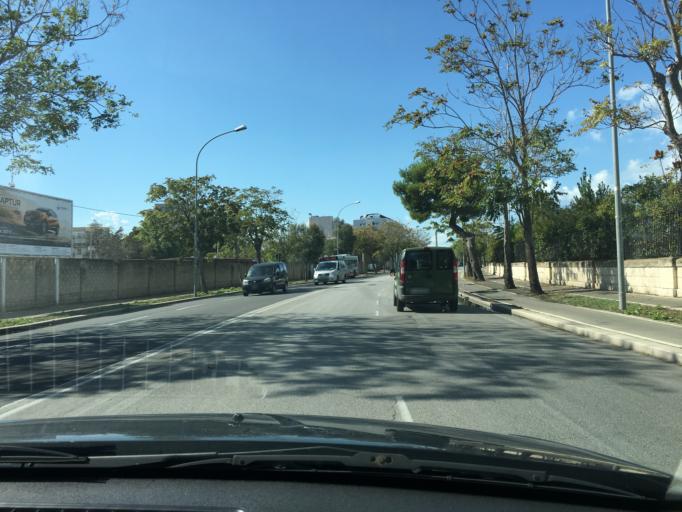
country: IT
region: Apulia
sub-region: Provincia di Bari
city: Bari
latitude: 41.1282
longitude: 16.8539
